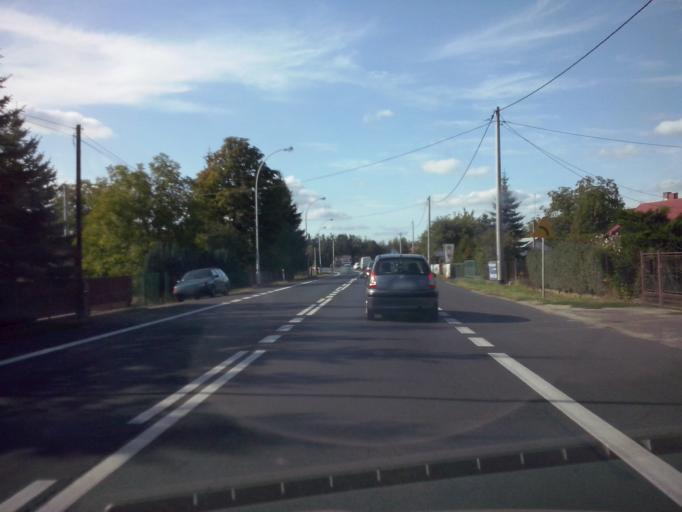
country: PL
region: Subcarpathian Voivodeship
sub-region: Powiat nizanski
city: Nisko
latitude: 50.5369
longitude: 22.1014
